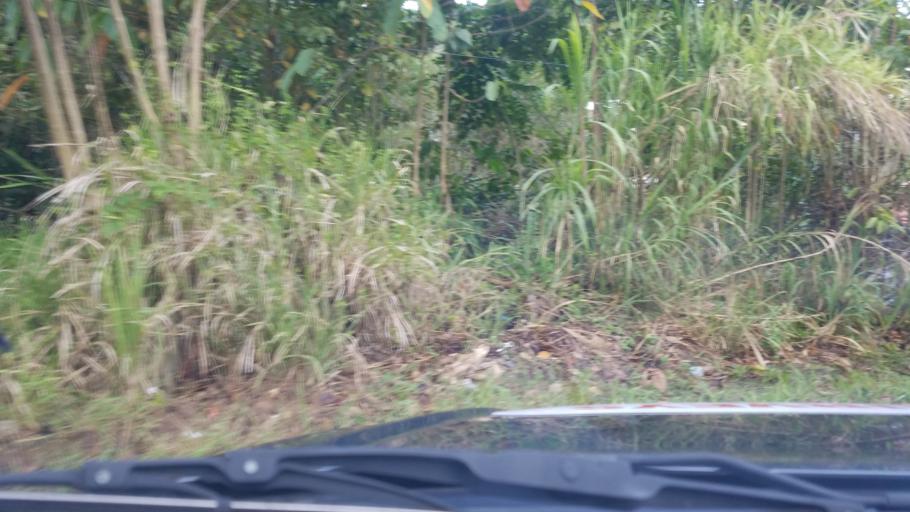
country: LC
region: Castries Quarter
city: Bisee
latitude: 14.0230
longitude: -60.9786
